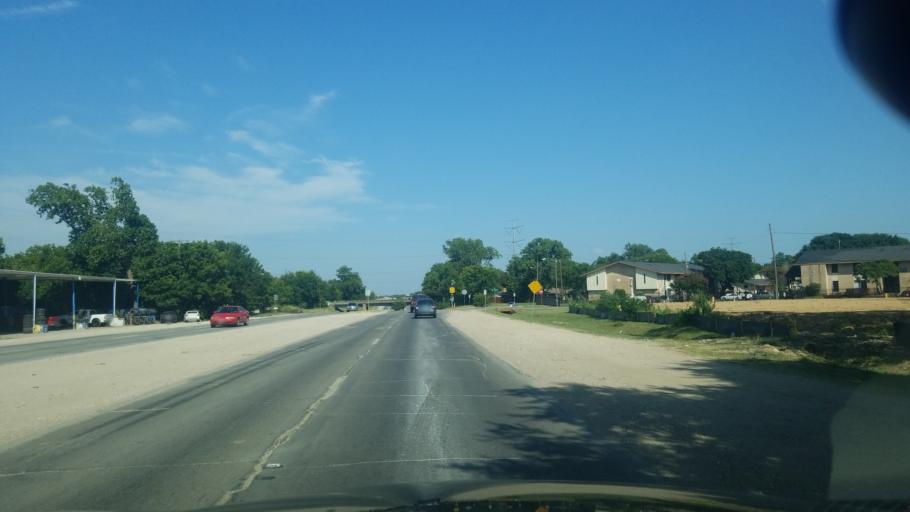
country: US
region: Texas
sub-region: Dallas County
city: Dallas
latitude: 32.7147
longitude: -96.7636
